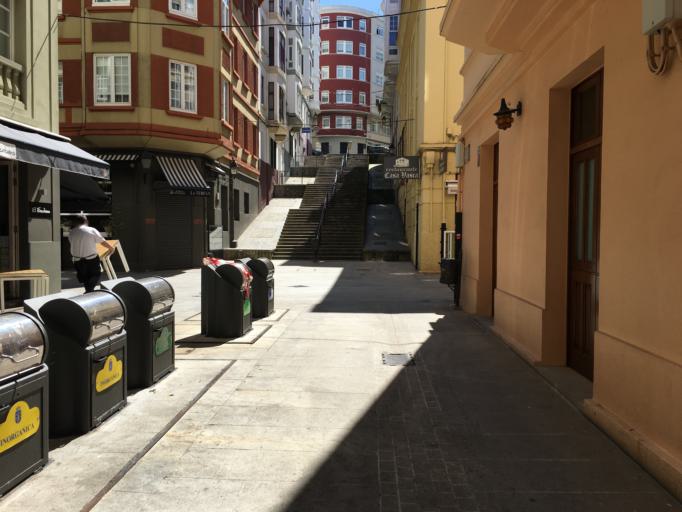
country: ES
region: Galicia
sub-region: Provincia da Coruna
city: A Coruna
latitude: 43.3709
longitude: -8.3953
